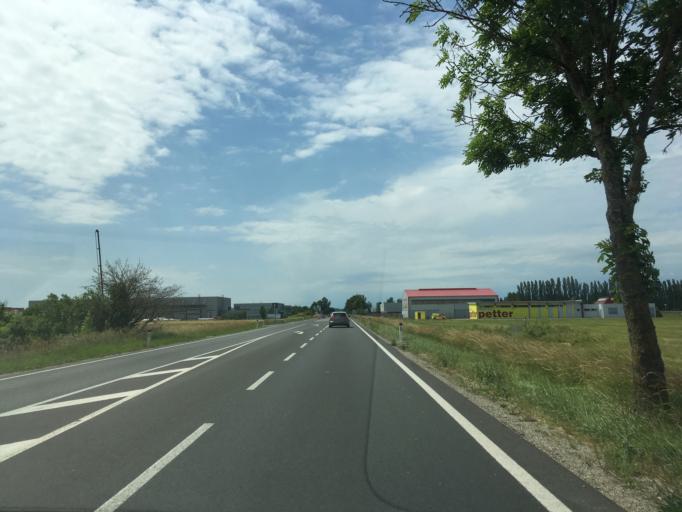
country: AT
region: Lower Austria
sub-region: Politischer Bezirk Baden
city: Teesdorf
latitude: 47.9680
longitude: 16.2763
